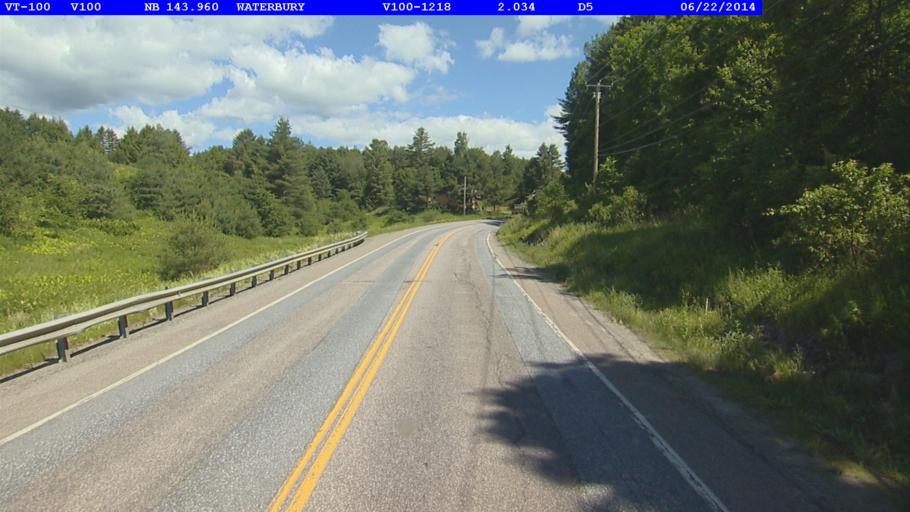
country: US
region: Vermont
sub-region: Washington County
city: Waterbury
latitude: 44.3609
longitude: -72.7329
